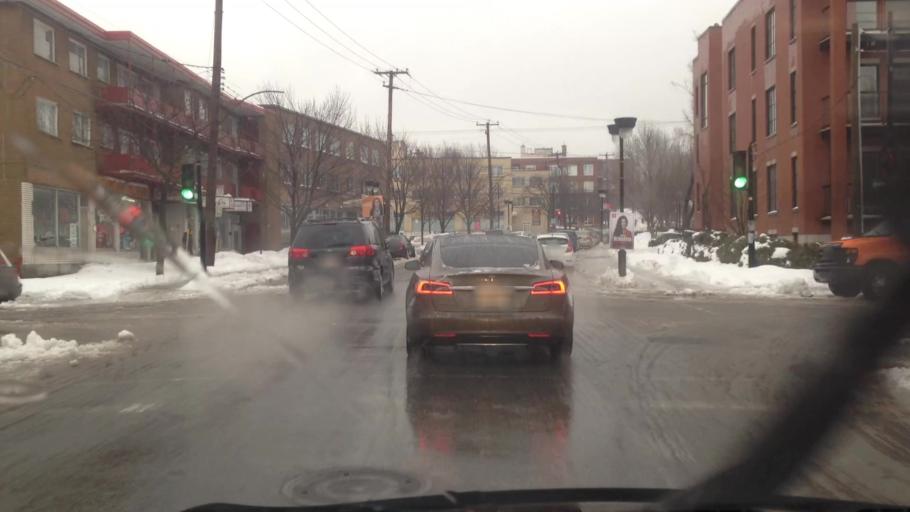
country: CA
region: Quebec
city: Mont-Royal
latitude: 45.5105
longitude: -73.6316
